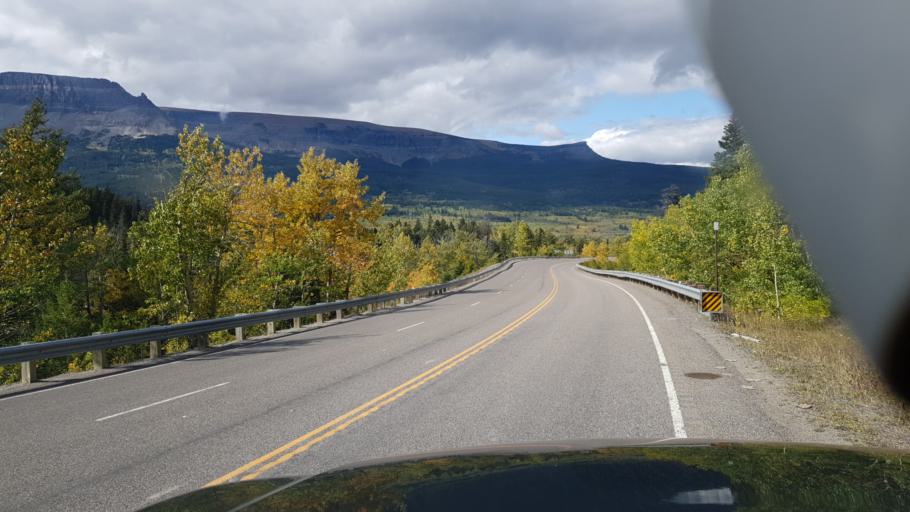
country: US
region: Montana
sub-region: Glacier County
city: North Browning
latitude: 48.7346
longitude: -113.4218
